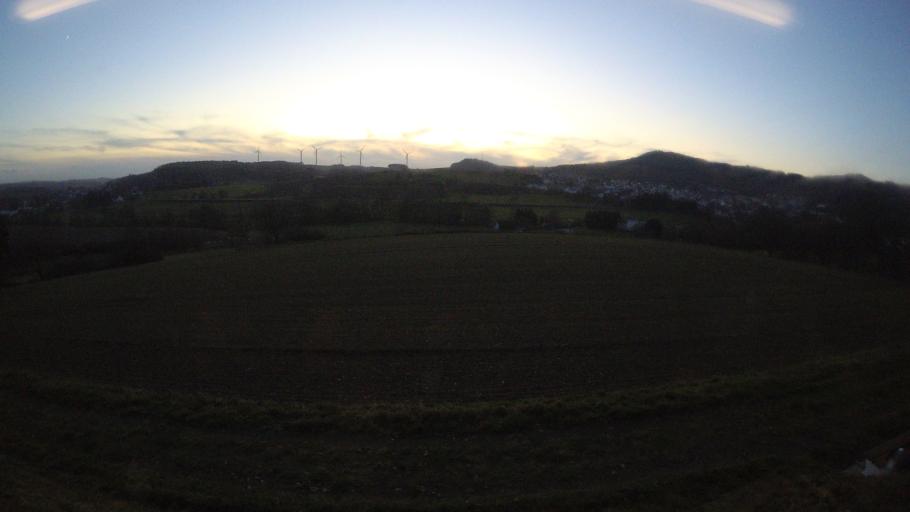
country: DE
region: Rheinland-Pfalz
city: Reichweiler
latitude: 49.5227
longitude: 7.2745
